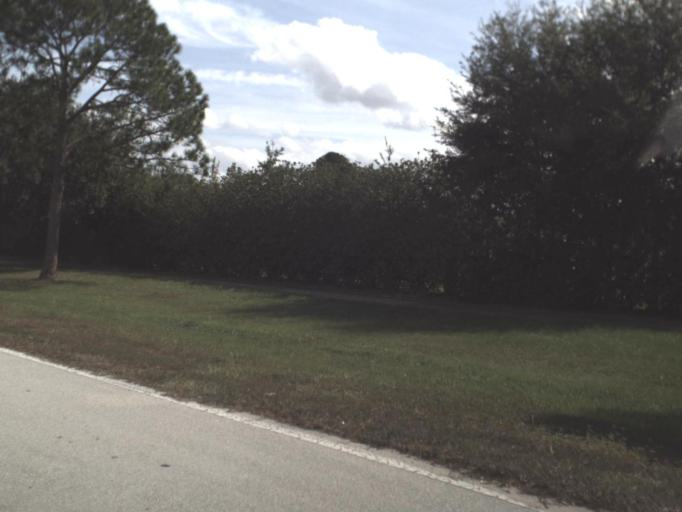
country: US
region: Florida
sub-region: Osceola County
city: Poinciana
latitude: 28.1456
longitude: -81.4561
